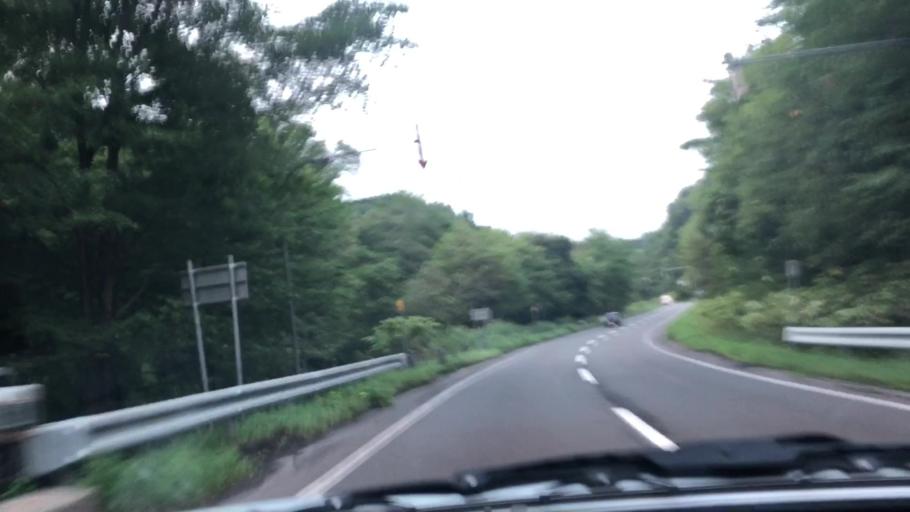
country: JP
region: Hokkaido
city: Chitose
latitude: 42.8917
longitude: 142.1230
